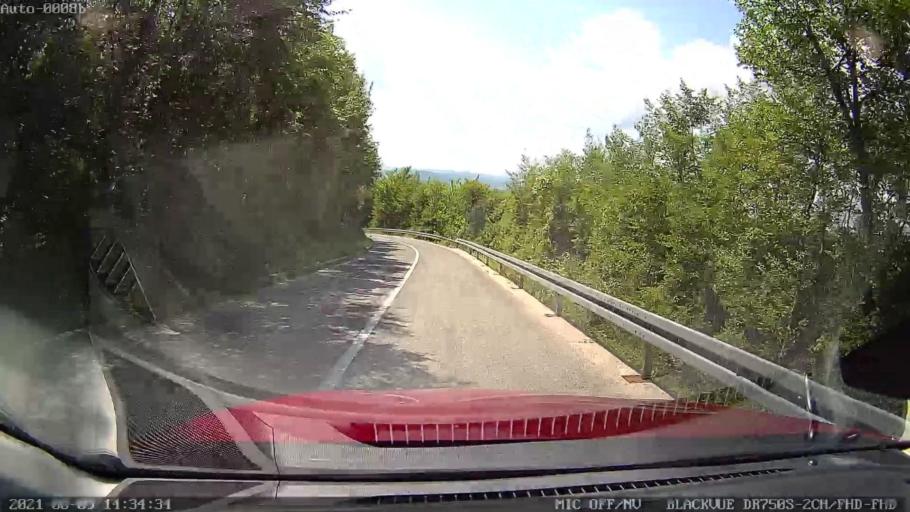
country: HR
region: Istarska
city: Lovran
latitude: 45.3138
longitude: 14.1834
